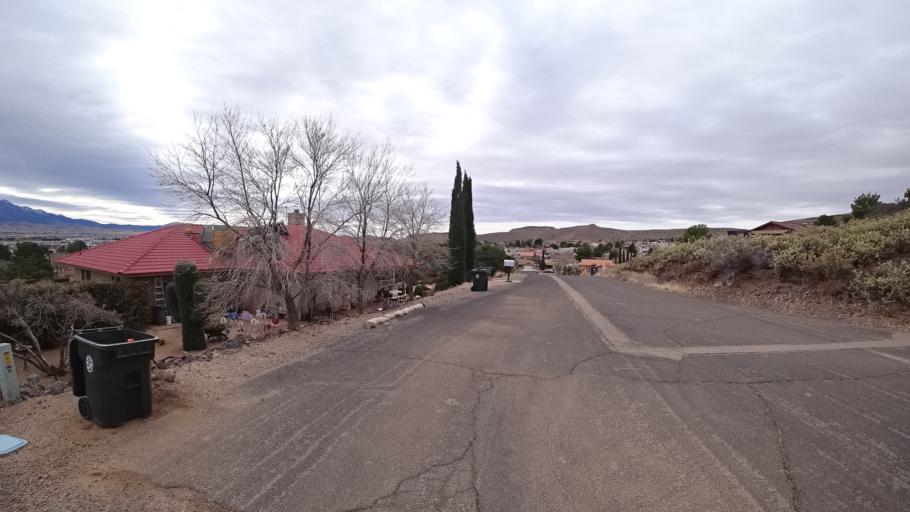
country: US
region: Arizona
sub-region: Mohave County
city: New Kingman-Butler
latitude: 35.2400
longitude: -114.0441
